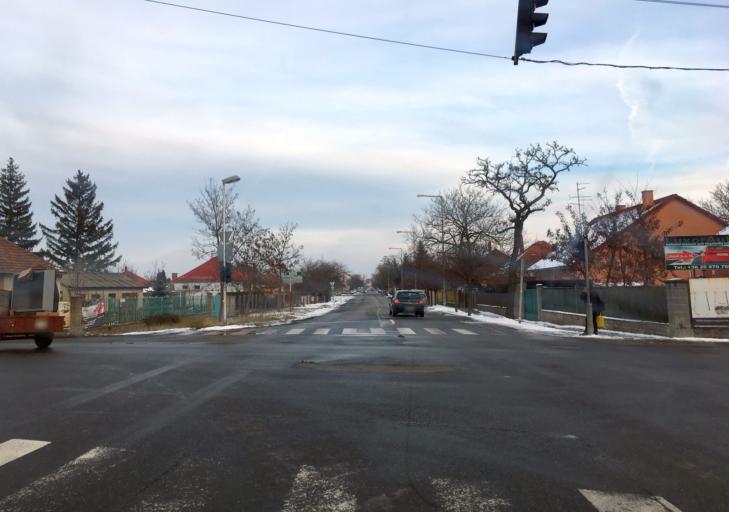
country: HU
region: Gyor-Moson-Sopron
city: Mosonmagyarovar
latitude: 47.8562
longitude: 17.2658
